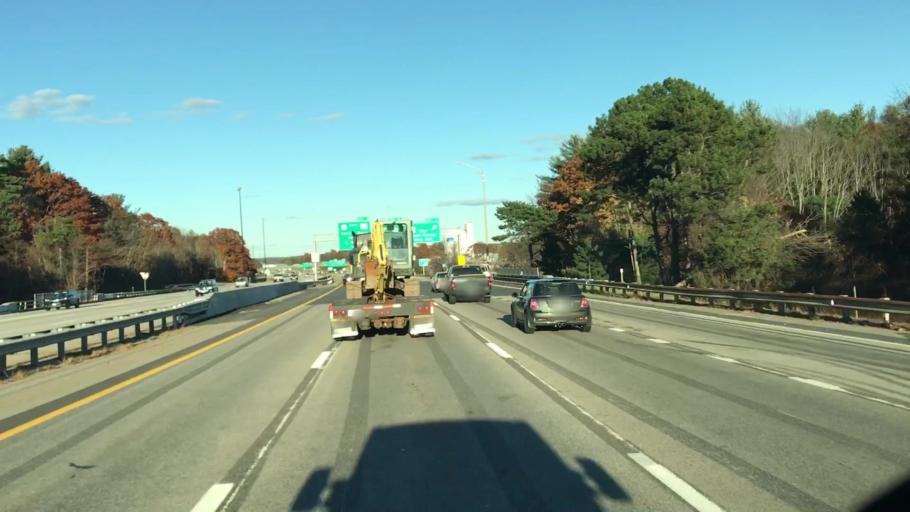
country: US
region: Maine
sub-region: York County
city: Kittery
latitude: 43.0979
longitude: -70.7569
